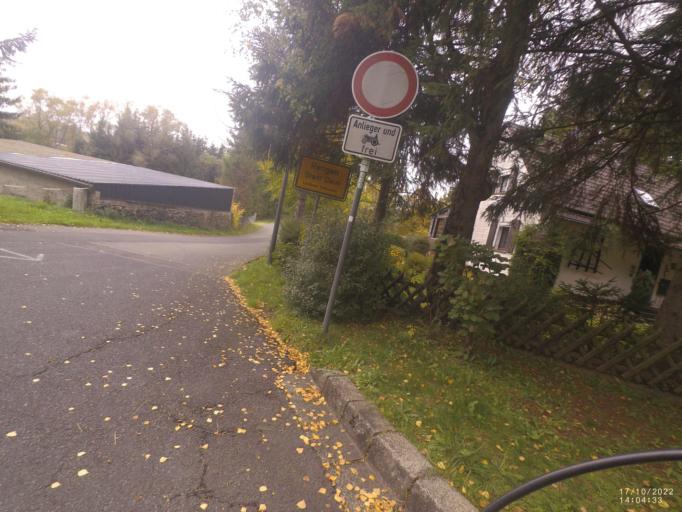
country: DE
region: Rheinland-Pfalz
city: Horscheid
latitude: 50.2246
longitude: 6.8485
